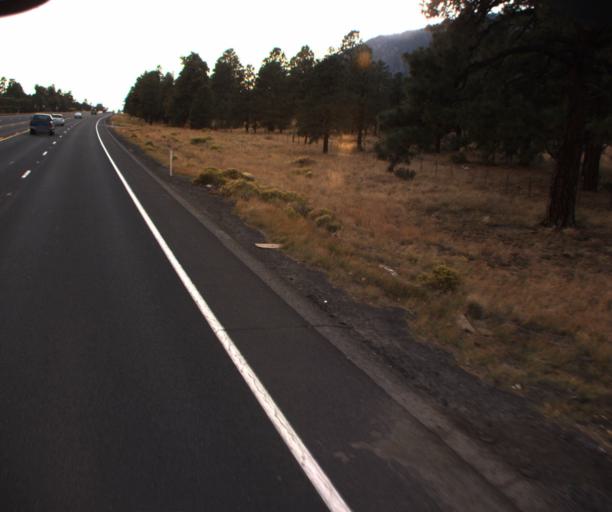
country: US
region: Arizona
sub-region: Coconino County
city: Flagstaff
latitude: 35.2498
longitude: -111.5601
